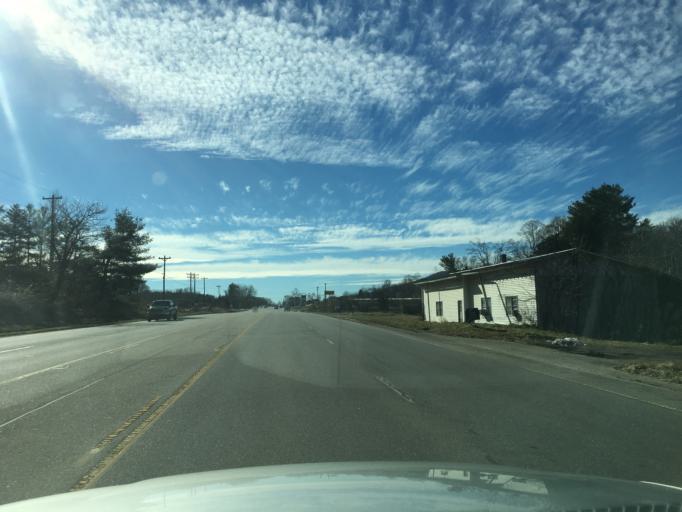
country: US
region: North Carolina
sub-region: Henderson County
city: Mills River
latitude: 35.3853
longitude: -82.5680
